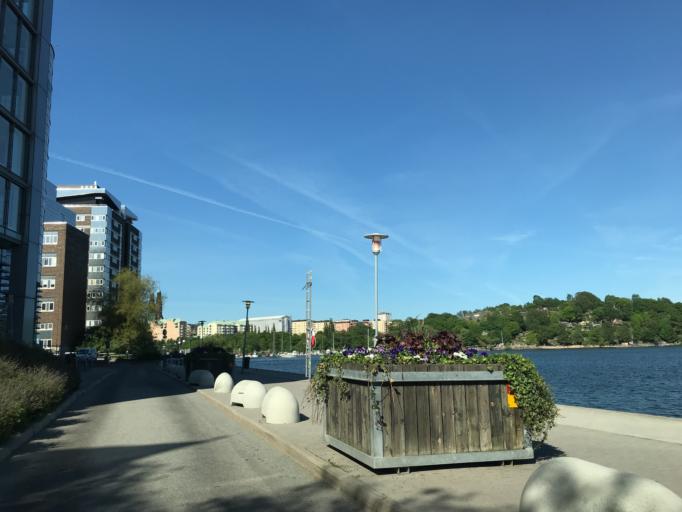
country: SE
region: Stockholm
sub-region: Stockholms Kommun
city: Arsta
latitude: 59.3102
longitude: 18.0314
